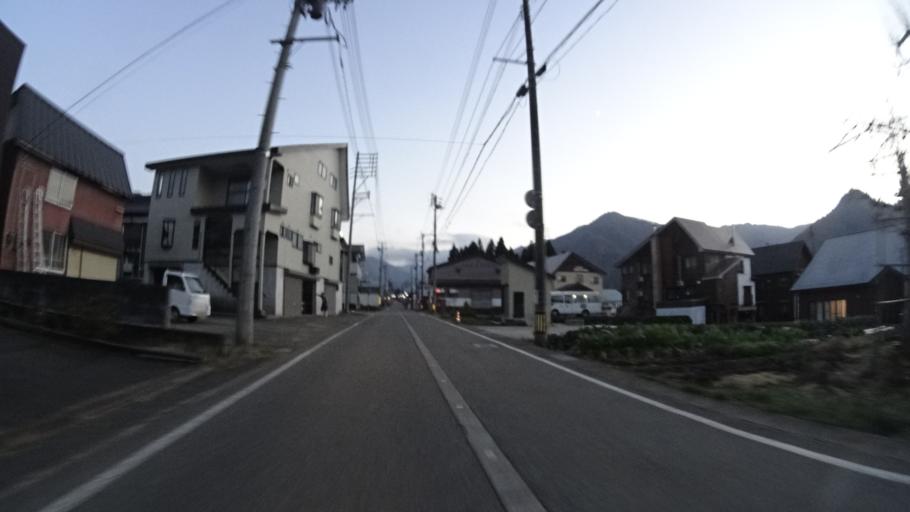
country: JP
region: Niigata
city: Shiozawa
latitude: 36.9139
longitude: 138.8459
